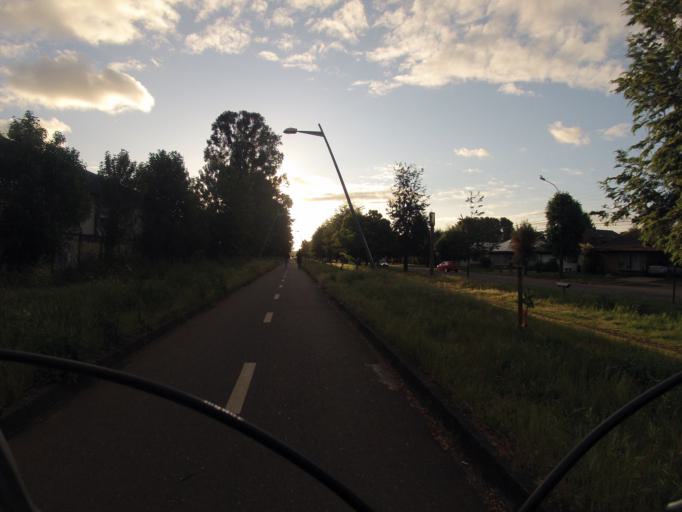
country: CL
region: Araucania
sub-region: Provincia de Cautin
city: Temuco
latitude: -38.7483
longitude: -72.6326
